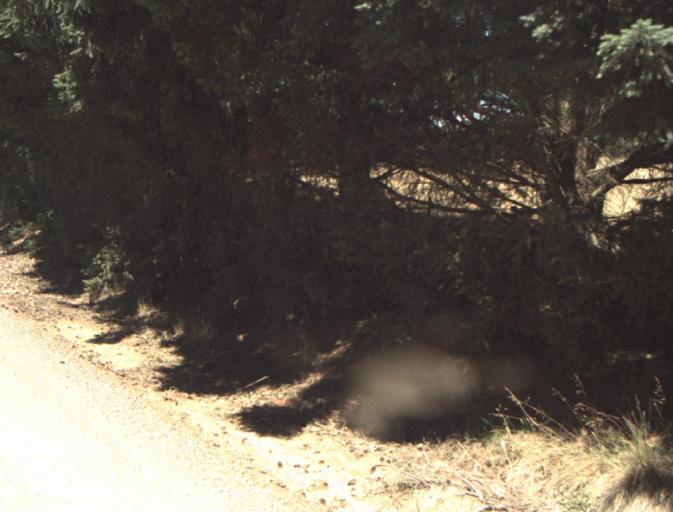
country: AU
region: Tasmania
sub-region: Dorset
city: Scottsdale
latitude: -41.3224
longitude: 147.4476
